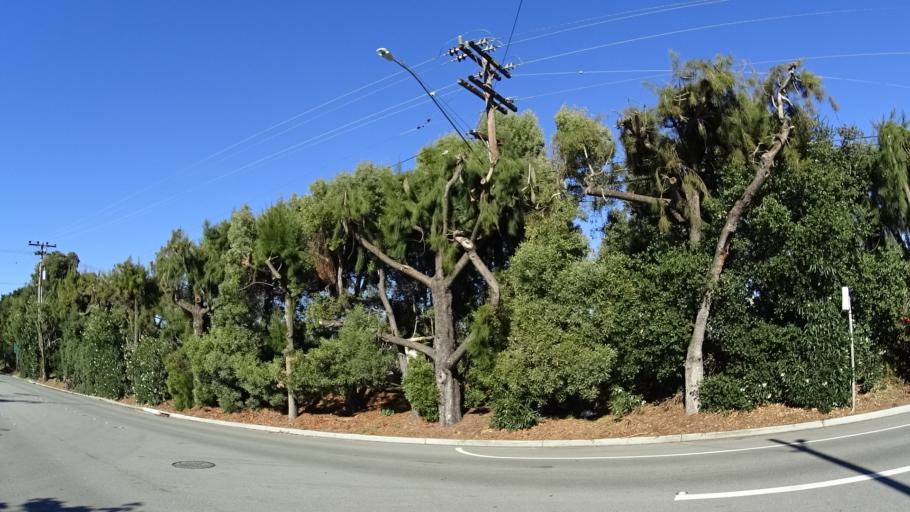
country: US
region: California
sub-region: San Mateo County
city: Millbrae
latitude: 37.5941
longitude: -122.3791
